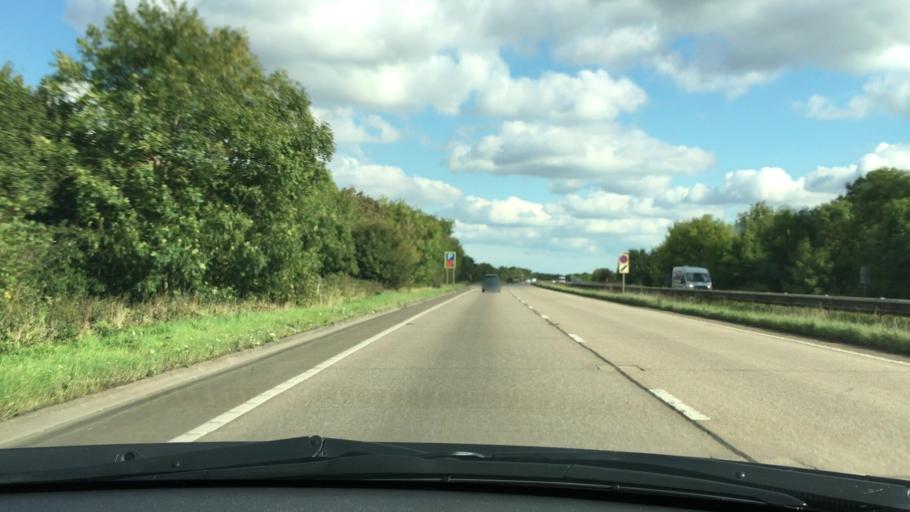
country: GB
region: England
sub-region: North East Lincolnshire
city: Healing
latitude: 53.5939
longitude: -0.1727
